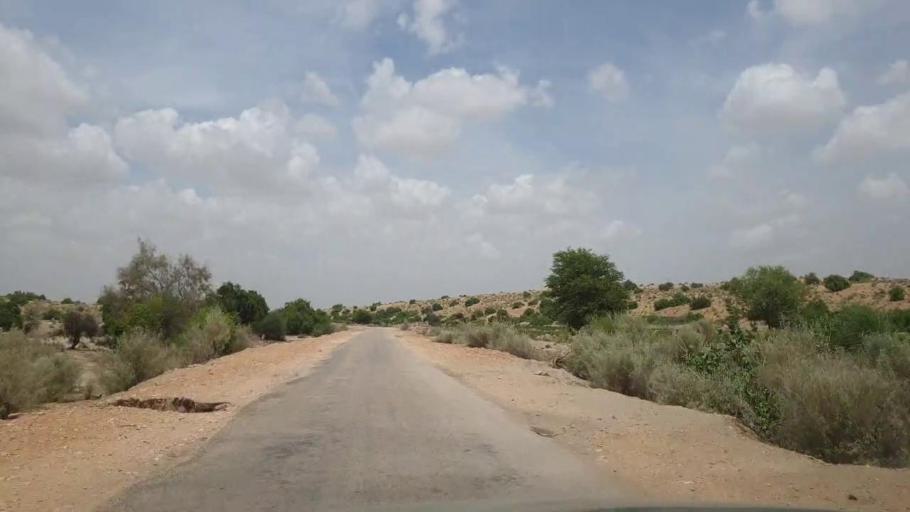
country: PK
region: Sindh
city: Kot Diji
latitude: 27.2106
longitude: 69.0962
